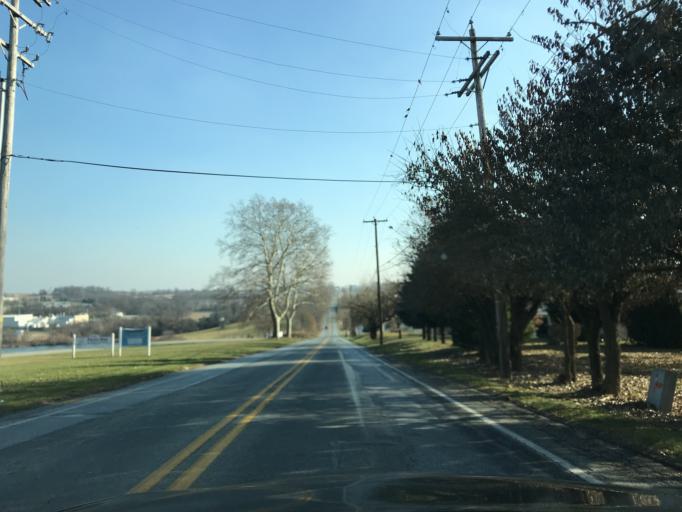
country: US
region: Pennsylvania
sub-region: York County
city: Loganville
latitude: 39.8212
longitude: -76.6947
